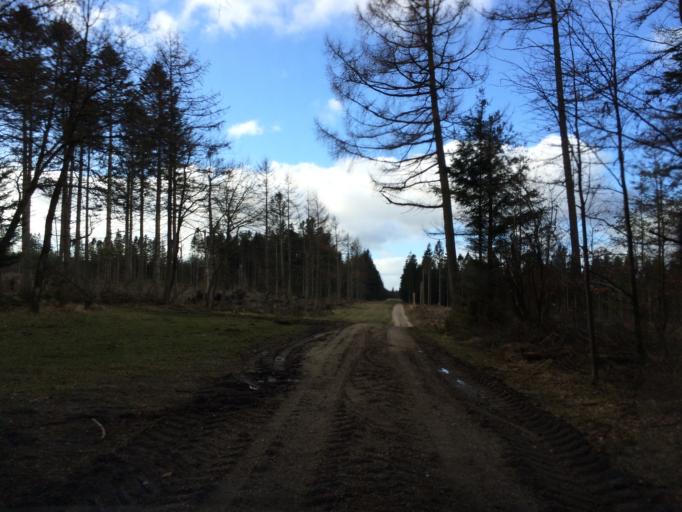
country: DK
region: Central Jutland
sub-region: Holstebro Kommune
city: Ulfborg
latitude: 56.2612
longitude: 8.4491
